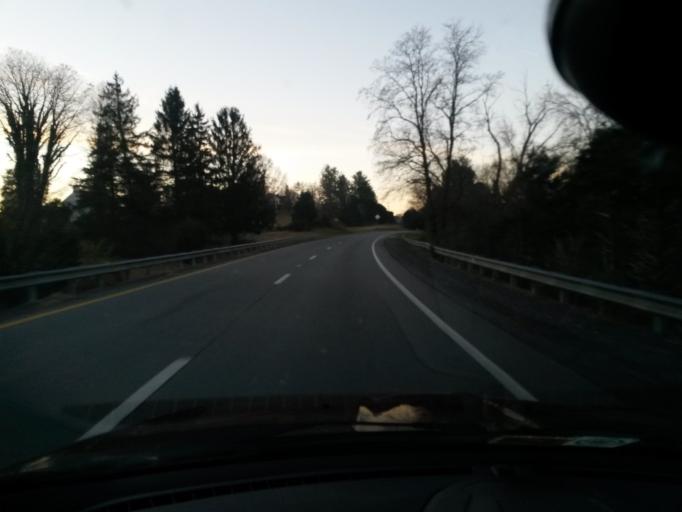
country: US
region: Virginia
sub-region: Botetourt County
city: Fincastle
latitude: 37.4910
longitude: -79.8776
